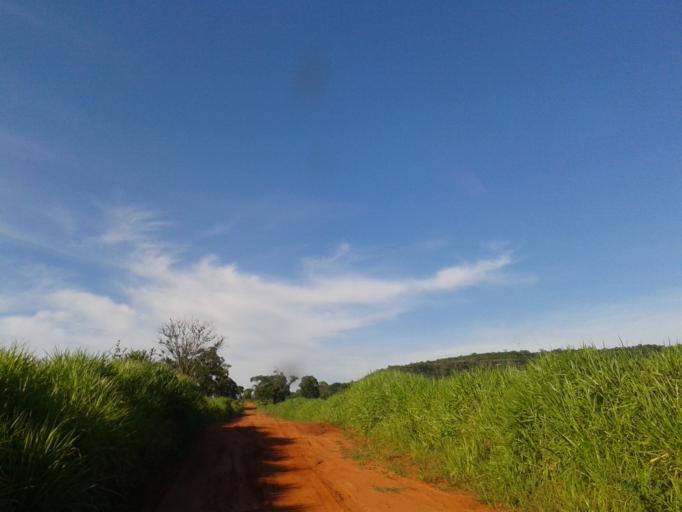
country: BR
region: Minas Gerais
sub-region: Santa Vitoria
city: Santa Vitoria
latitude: -19.0855
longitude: -49.9628
